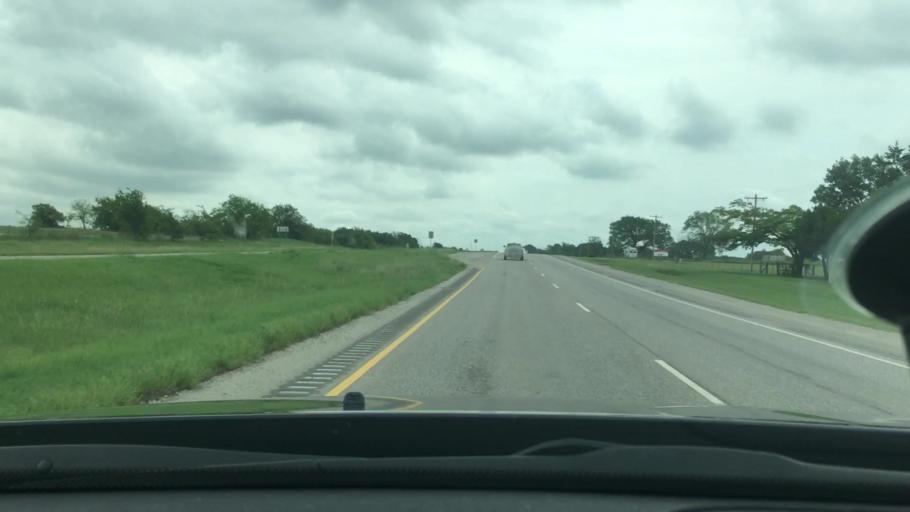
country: US
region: Oklahoma
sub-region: Carter County
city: Wilson
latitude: 34.1729
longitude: -97.4735
